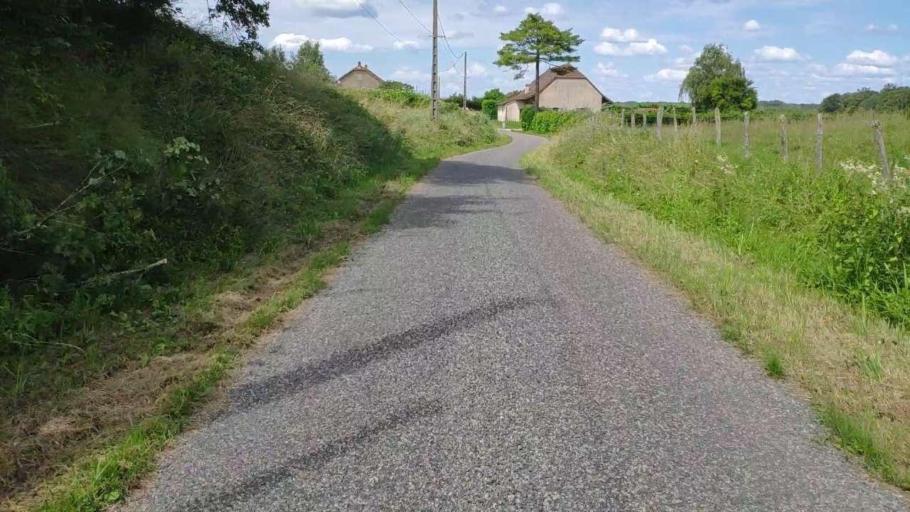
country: FR
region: Franche-Comte
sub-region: Departement du Jura
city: Bletterans
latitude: 46.8214
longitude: 5.4505
